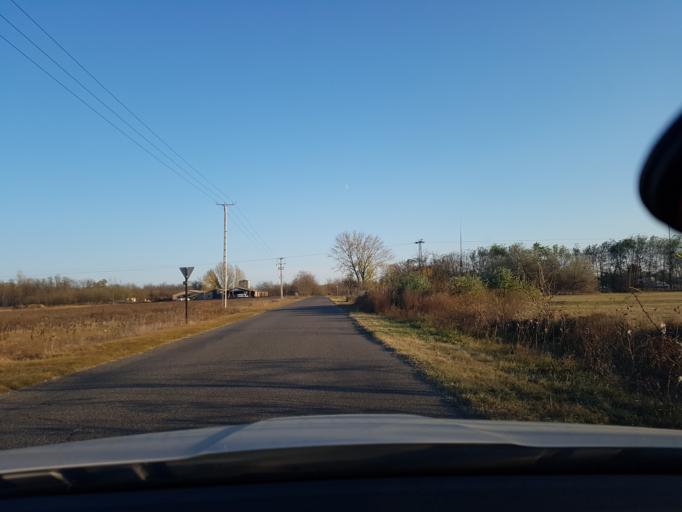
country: HU
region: Bacs-Kiskun
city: Lajosmizse
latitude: 47.0482
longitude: 19.5784
